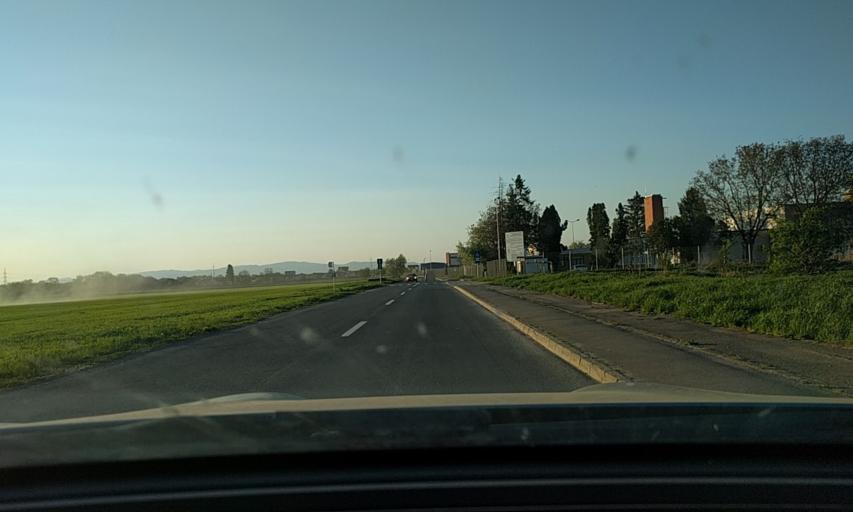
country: RO
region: Brasov
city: Brasov
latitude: 45.6800
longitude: 25.5727
